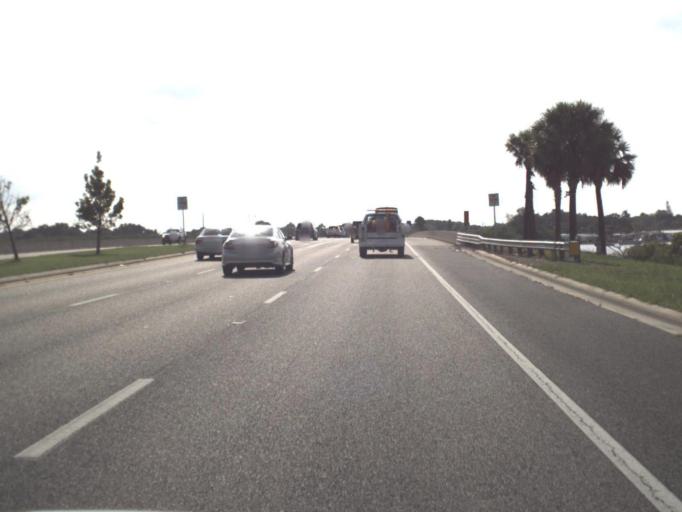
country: US
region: Florida
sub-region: Manatee County
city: Ellenton
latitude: 27.4973
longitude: -82.5229
